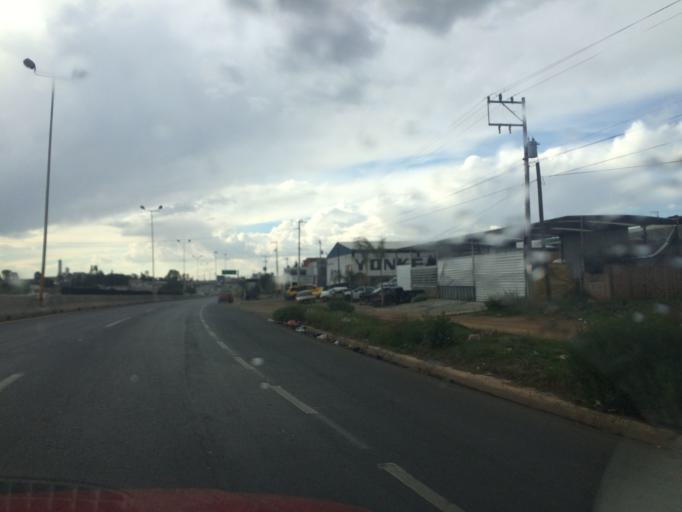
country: MX
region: Zacatecas
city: Zacatecas
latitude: 22.7655
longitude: -102.6111
